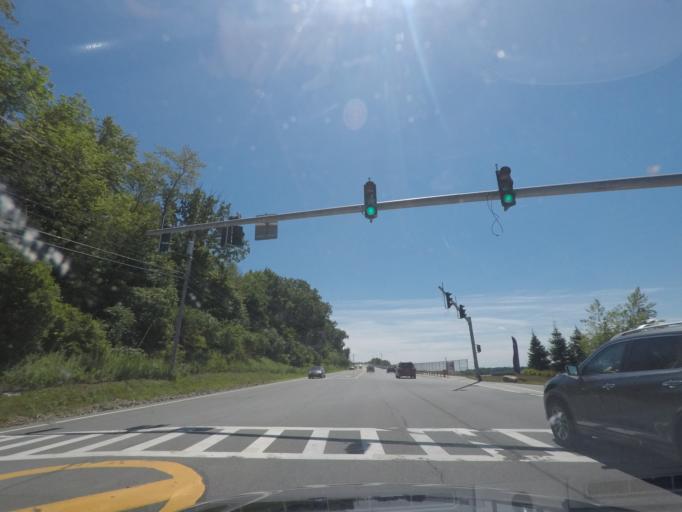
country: US
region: New York
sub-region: Rensselaer County
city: Hampton Manor
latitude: 42.6389
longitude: -73.7000
